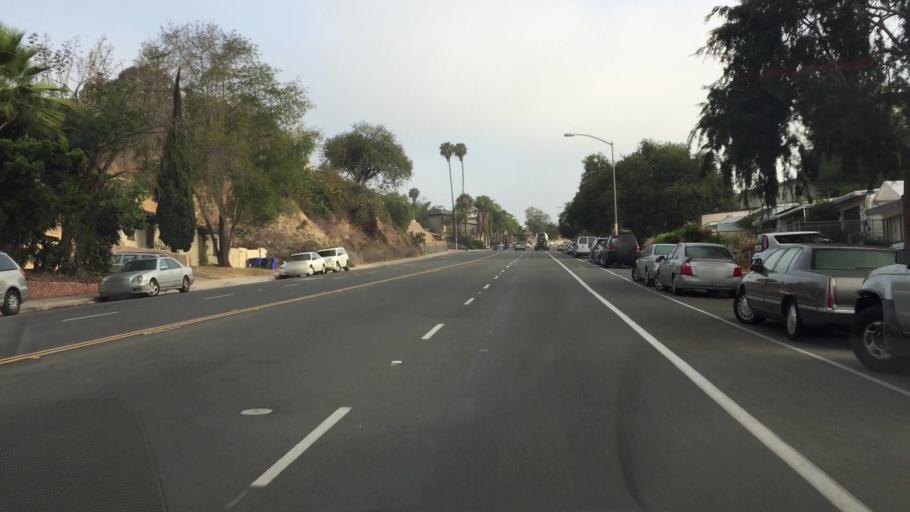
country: US
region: California
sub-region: San Diego County
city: Lemon Grove
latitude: 32.7543
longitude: -117.0652
